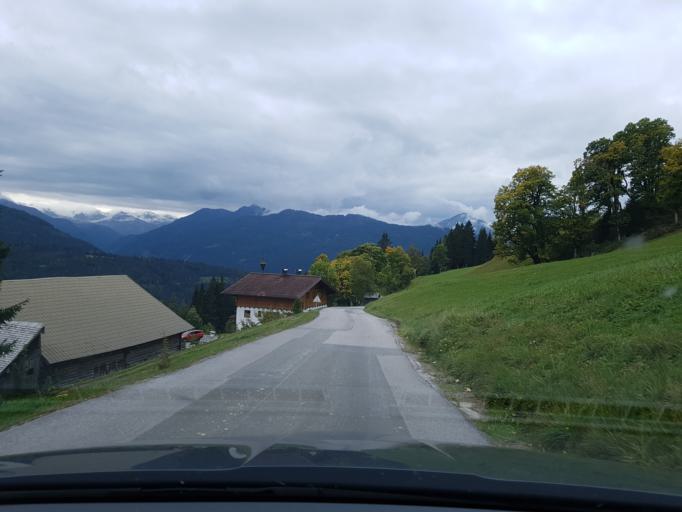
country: AT
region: Salzburg
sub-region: Politischer Bezirk Sankt Johann im Pongau
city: Filzmoos
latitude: 47.4008
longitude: 13.4981
